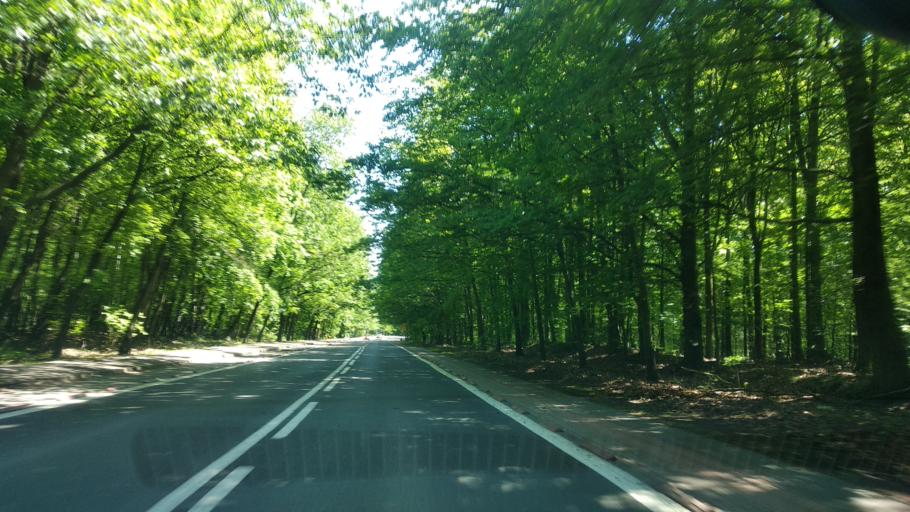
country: PL
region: Silesian Voivodeship
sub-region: Ruda Slaska
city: Ruda Slaska
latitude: 50.2358
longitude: 18.9114
